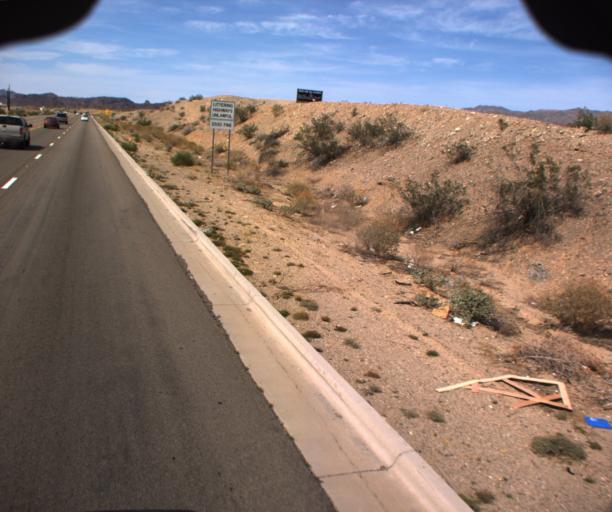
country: US
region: Arizona
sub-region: Mohave County
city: Desert Hills
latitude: 34.5234
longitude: -114.3494
